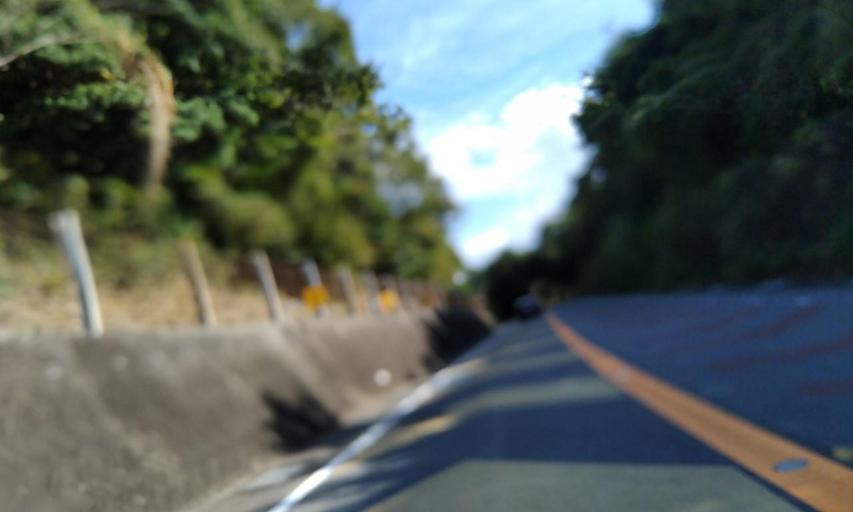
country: JP
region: Wakayama
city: Tanabe
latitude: 33.7803
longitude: 135.2988
